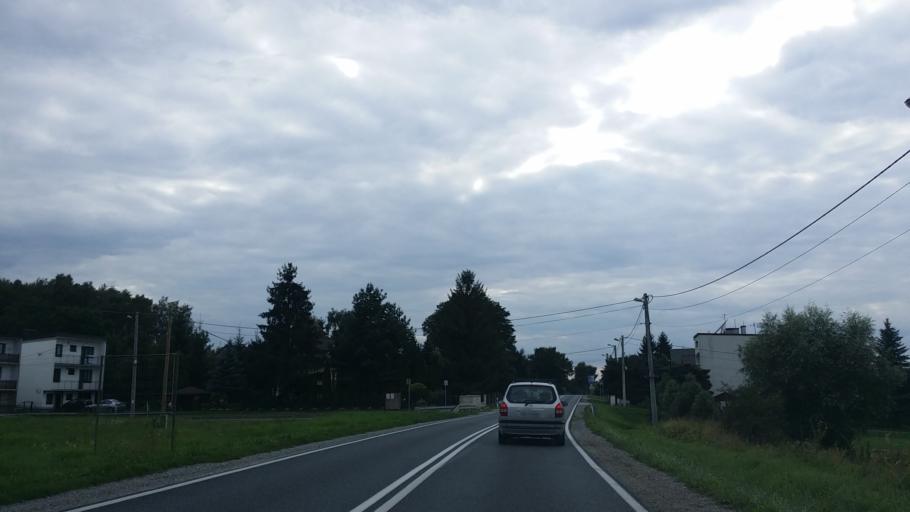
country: PL
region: Lesser Poland Voivodeship
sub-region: Powiat krakowski
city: Krzecin
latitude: 49.9588
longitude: 19.7429
